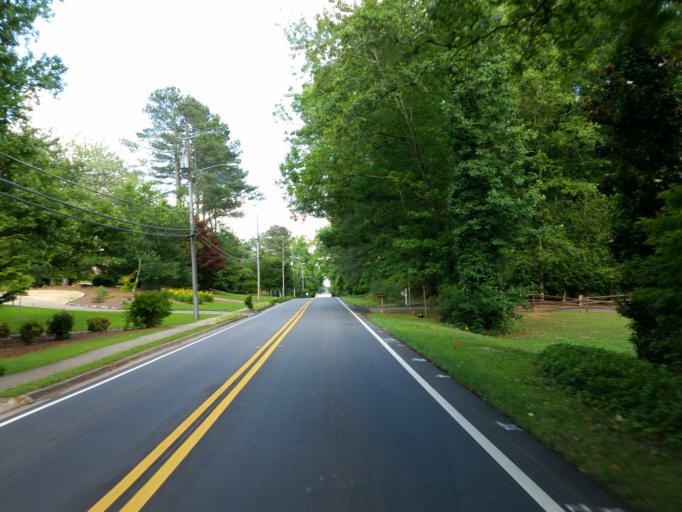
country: US
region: Georgia
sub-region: Fulton County
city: Roswell
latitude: 34.0613
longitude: -84.3581
